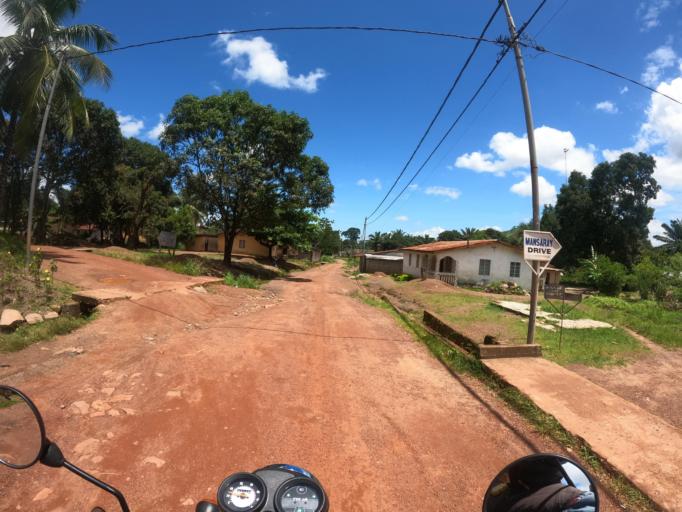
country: SL
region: Northern Province
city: Makeni
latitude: 8.8938
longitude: -12.0604
